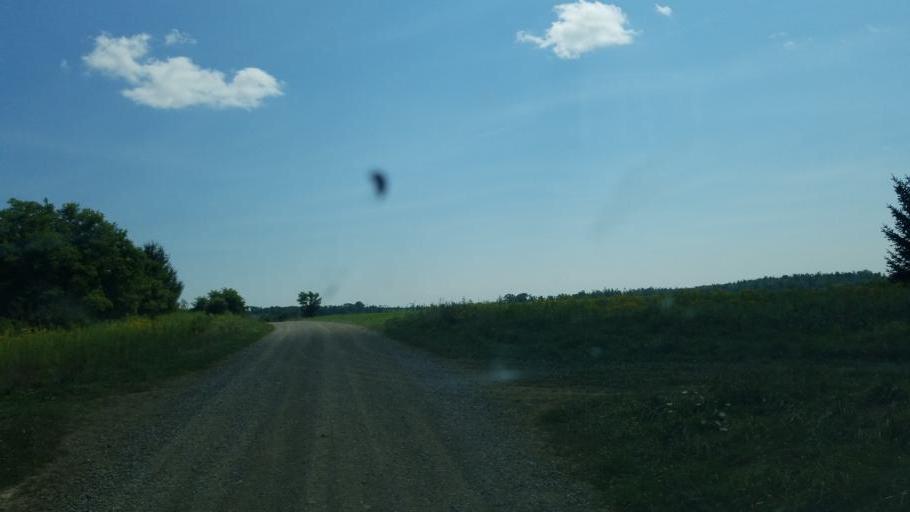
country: US
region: Pennsylvania
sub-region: Clarion County
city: Knox
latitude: 41.1089
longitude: -79.5332
